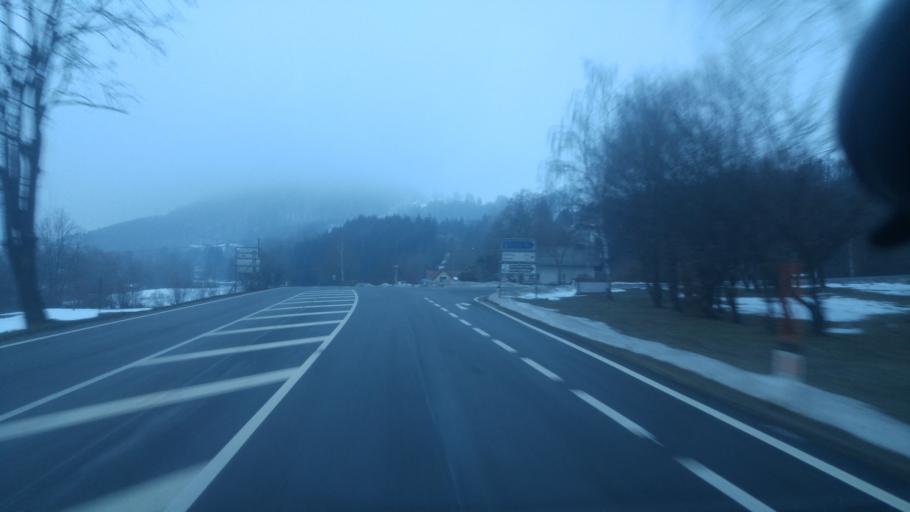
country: AT
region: Lower Austria
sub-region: Politischer Bezirk Baden
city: Altenmarkt an der Triesting
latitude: 48.0141
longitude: 16.0067
